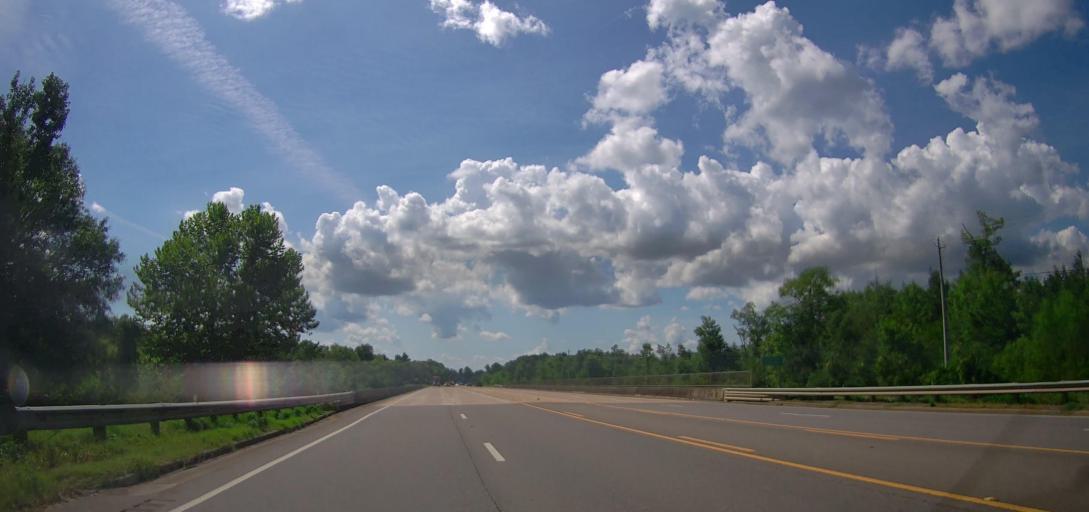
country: US
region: Alabama
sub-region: Pickens County
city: Reform
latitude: 33.3735
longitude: -88.0026
